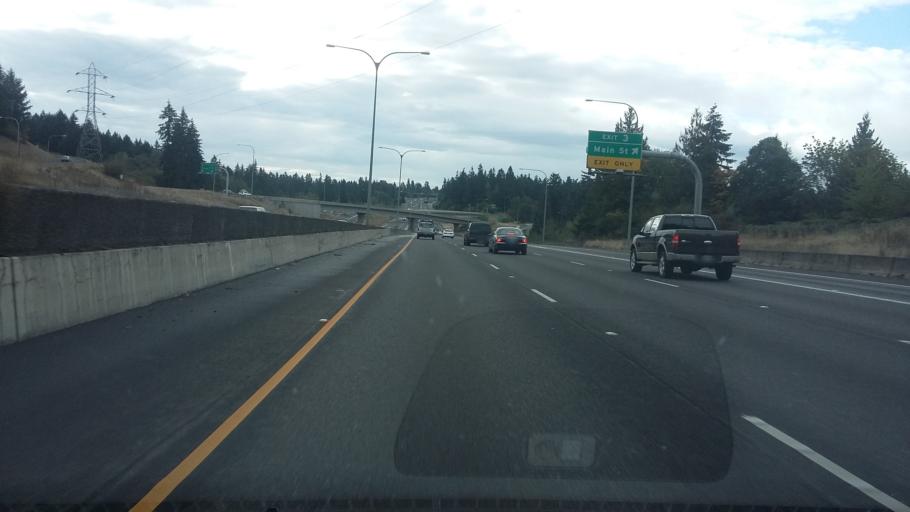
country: US
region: Washington
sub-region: Clark County
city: Hazel Dell
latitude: 45.6632
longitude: -122.6671
